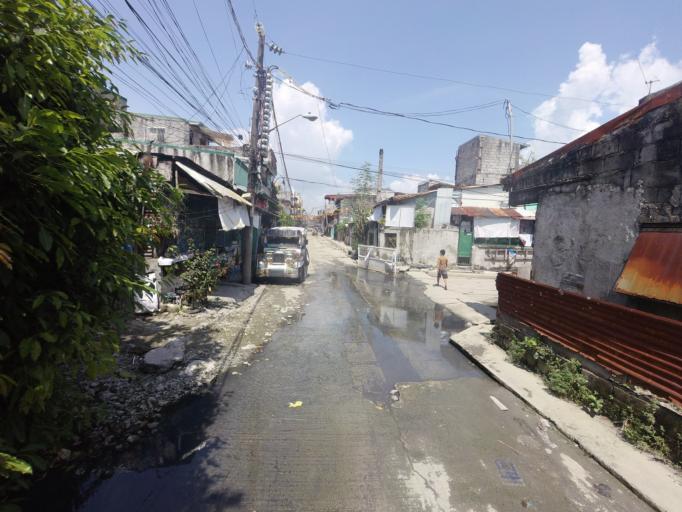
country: PH
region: Calabarzon
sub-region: Province of Rizal
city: Taytay
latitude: 14.5426
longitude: 121.1064
